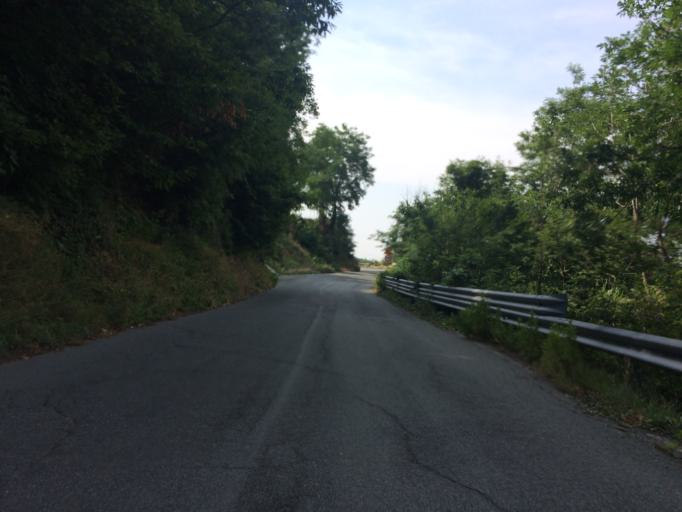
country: IT
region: Liguria
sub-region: Provincia di Savona
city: San Giovanni
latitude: 44.3927
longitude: 8.5105
